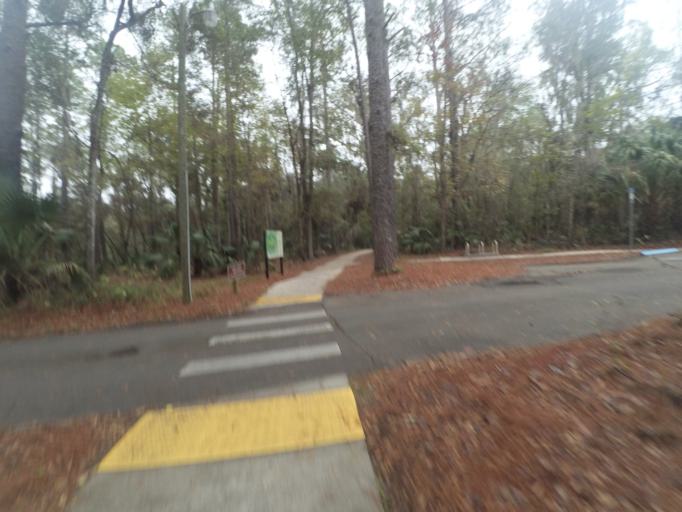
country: US
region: Florida
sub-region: Alachua County
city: Gainesville
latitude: 29.5473
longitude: -82.2925
